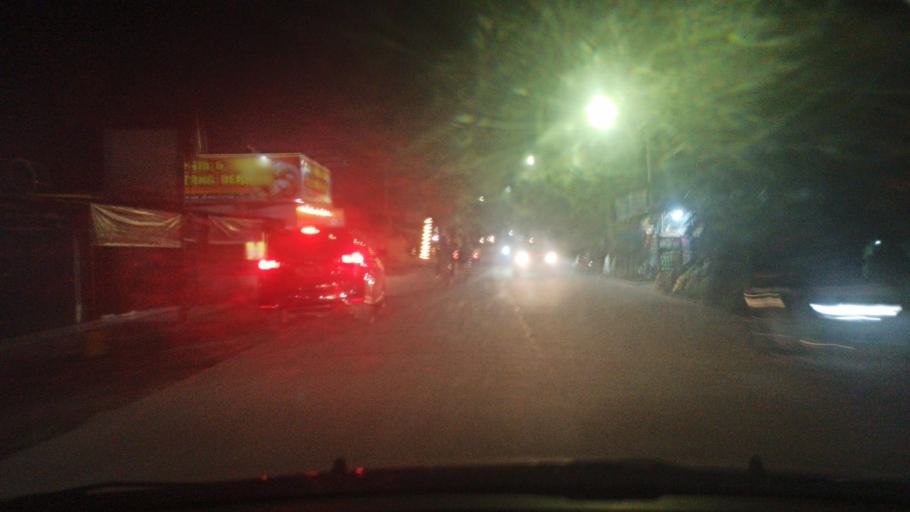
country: ID
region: South Sumatra
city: Plaju
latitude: -2.9456
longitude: 104.7853
